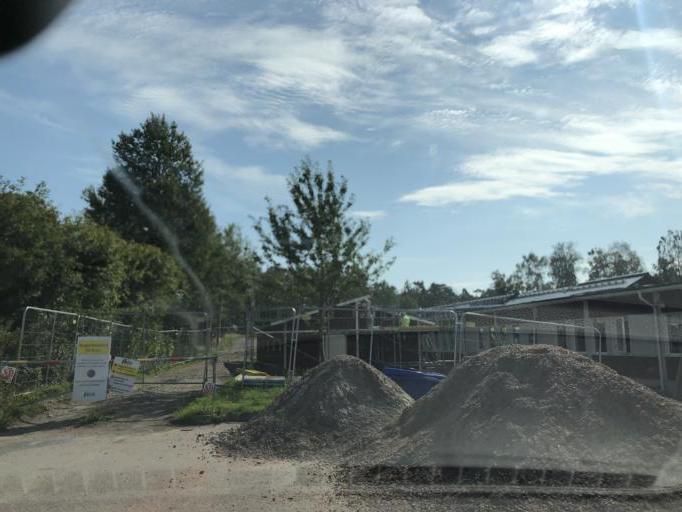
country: SE
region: Vaestra Goetaland
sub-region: Goteborg
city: Goeteborg
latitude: 57.7611
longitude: 11.9702
